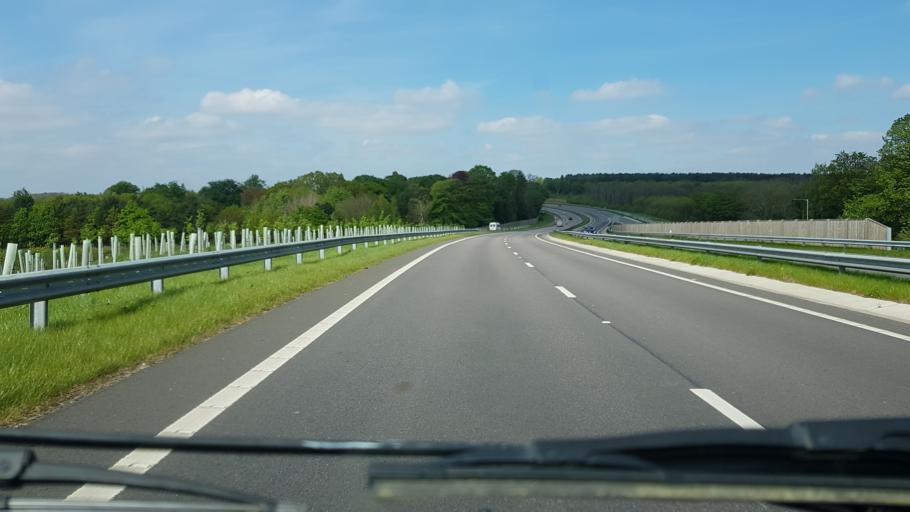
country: GB
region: England
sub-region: Kent
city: Pembury
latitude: 51.1568
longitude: 0.3035
